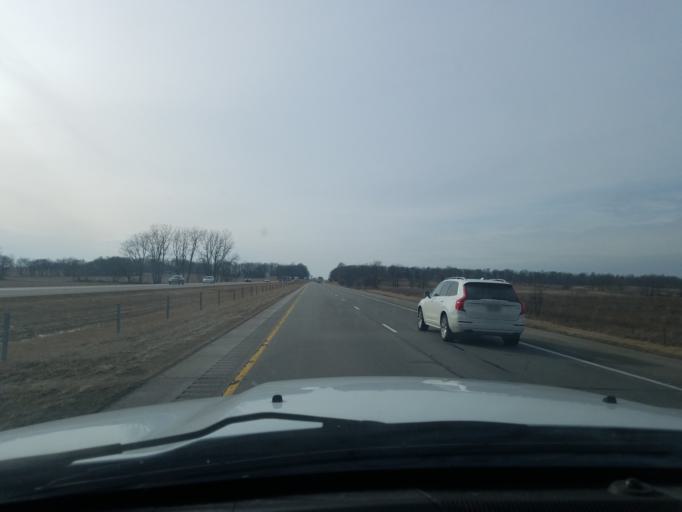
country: US
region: Indiana
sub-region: Henry County
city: New Castle
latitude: 39.8532
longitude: -85.3552
